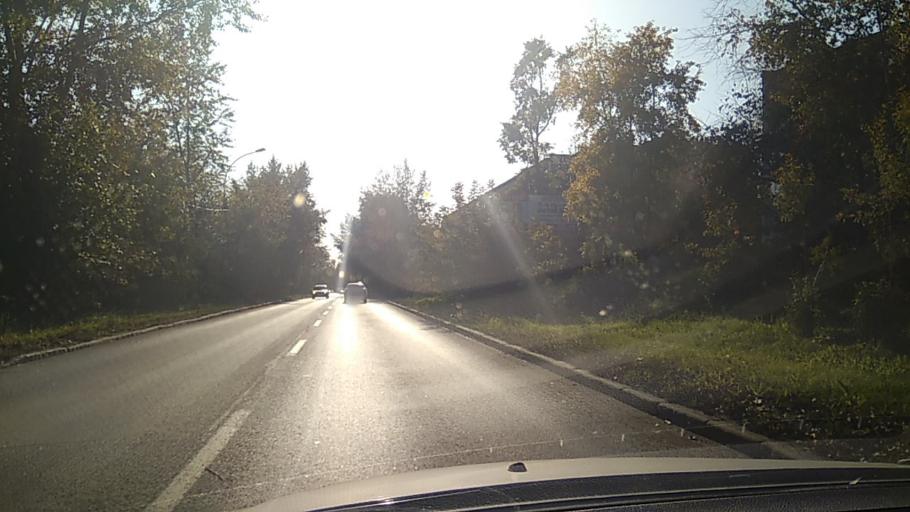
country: RU
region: Sverdlovsk
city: Yekaterinburg
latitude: 56.7760
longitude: 60.6379
